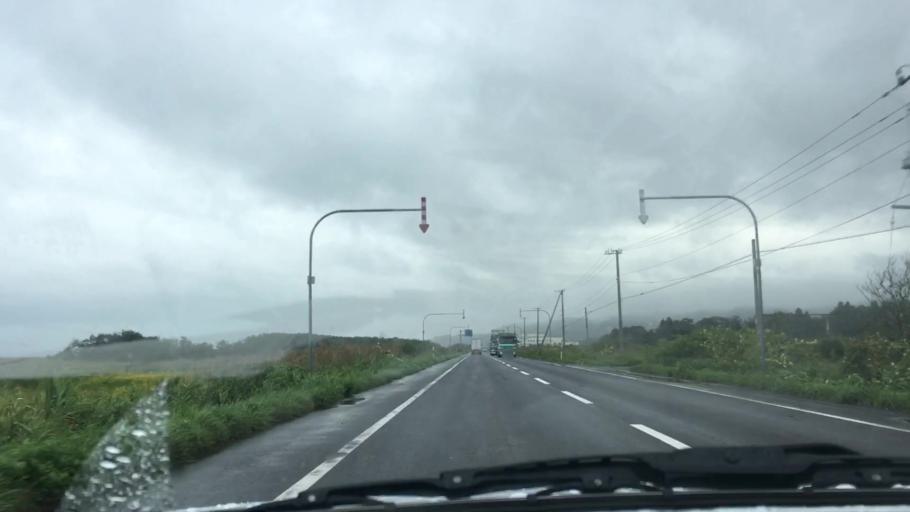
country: JP
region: Hokkaido
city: Niseko Town
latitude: 42.3943
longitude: 140.3001
